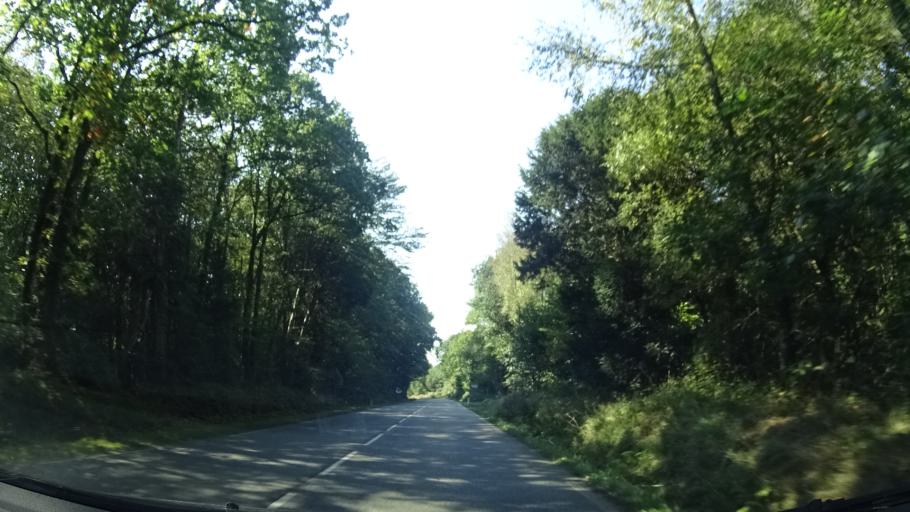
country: FR
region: Brittany
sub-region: Departement du Finistere
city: Cast
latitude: 48.1679
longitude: -4.1254
